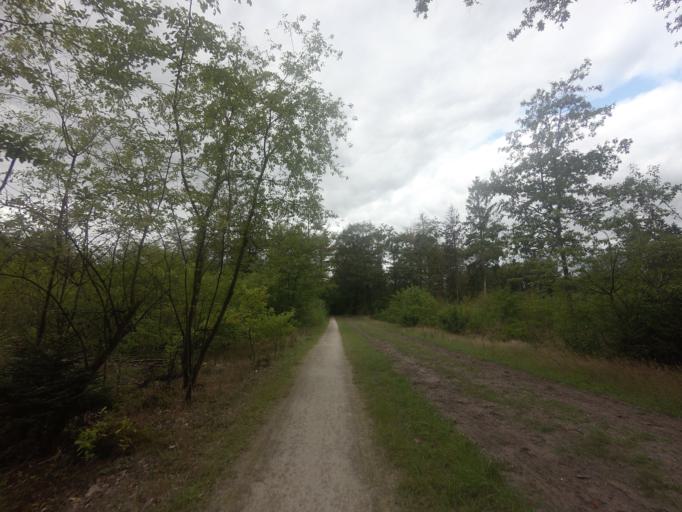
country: NL
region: Drenthe
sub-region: Gemeente Westerveld
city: Dwingeloo
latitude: 52.9236
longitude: 6.3246
